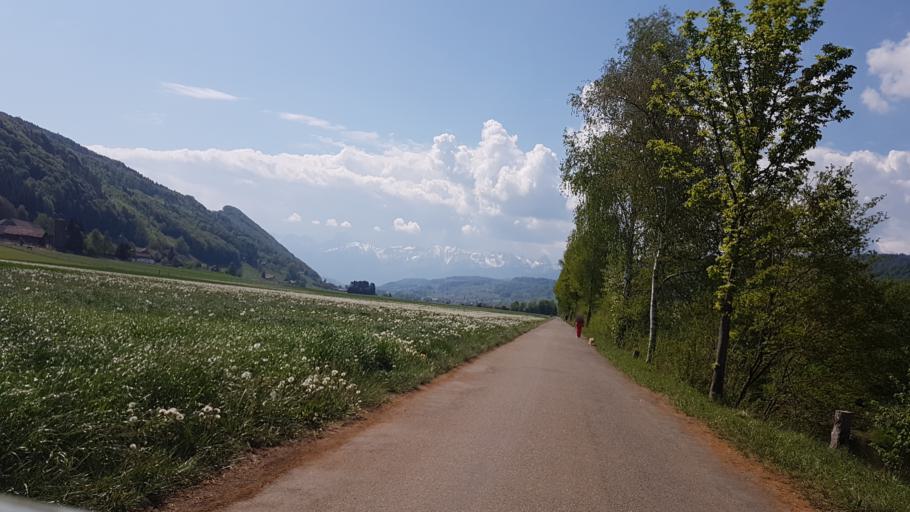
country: CH
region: Bern
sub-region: Bern-Mittelland District
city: Belp
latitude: 46.8798
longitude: 7.5004
